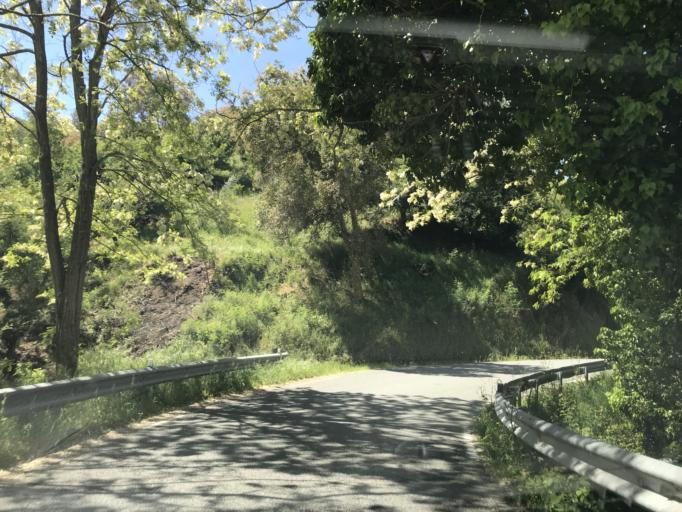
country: FR
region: Provence-Alpes-Cote d'Azur
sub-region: Departement des Alpes-Maritimes
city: Auribeau-sur-Siagne
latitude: 43.5852
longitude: 6.8985
